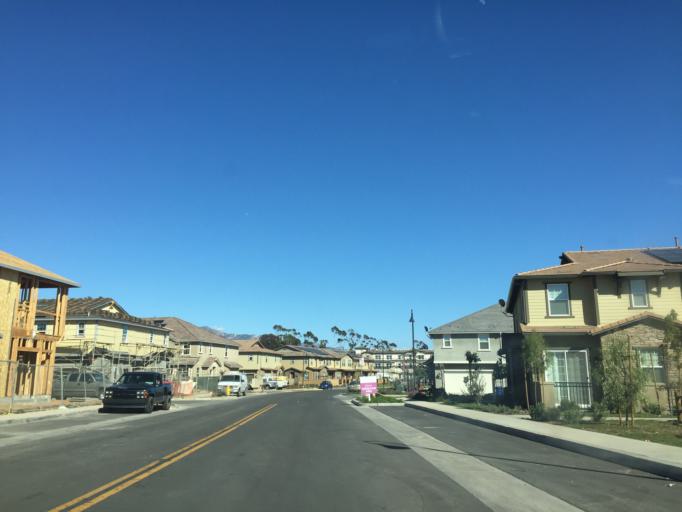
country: US
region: California
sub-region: Santa Barbara County
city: Isla Vista
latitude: 34.4357
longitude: -119.8565
